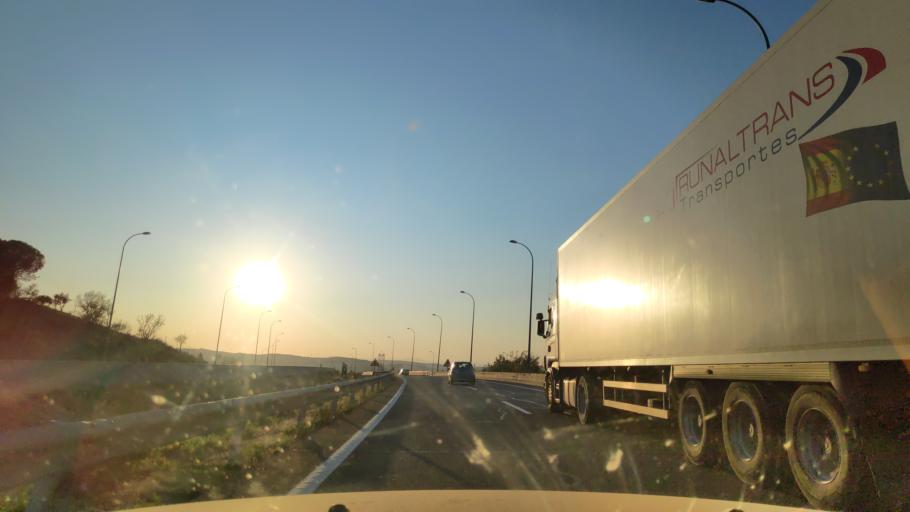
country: ES
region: Madrid
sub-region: Provincia de Madrid
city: Arganda
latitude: 40.2949
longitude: -3.4643
